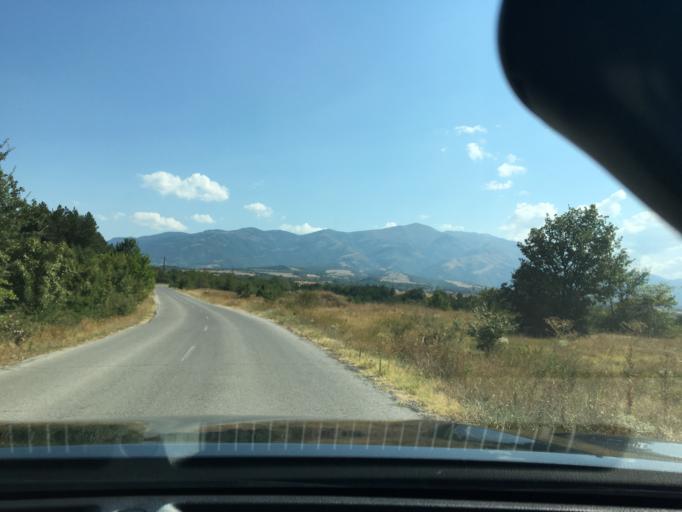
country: BG
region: Kyustendil
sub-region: Obshtina Boboshevo
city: Boboshevo
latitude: 42.1398
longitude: 23.0671
